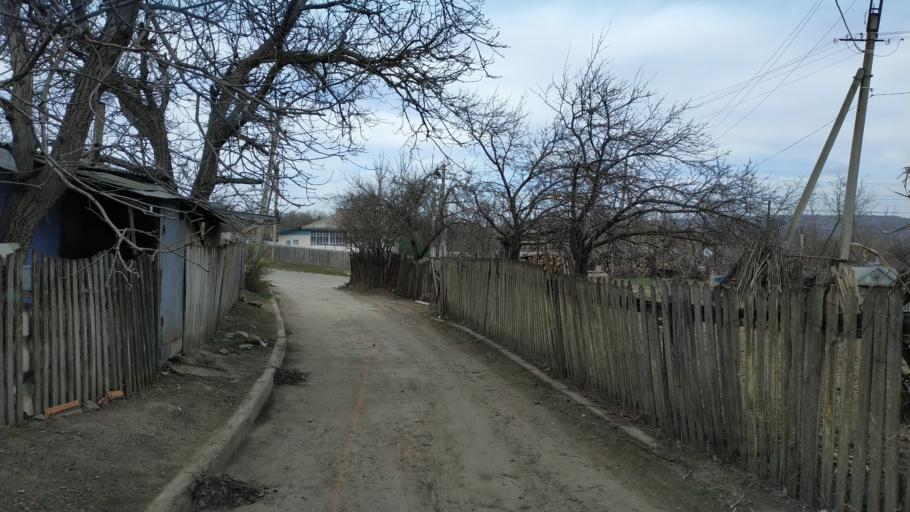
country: MD
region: Hincesti
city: Dancu
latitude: 46.9259
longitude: 28.2624
